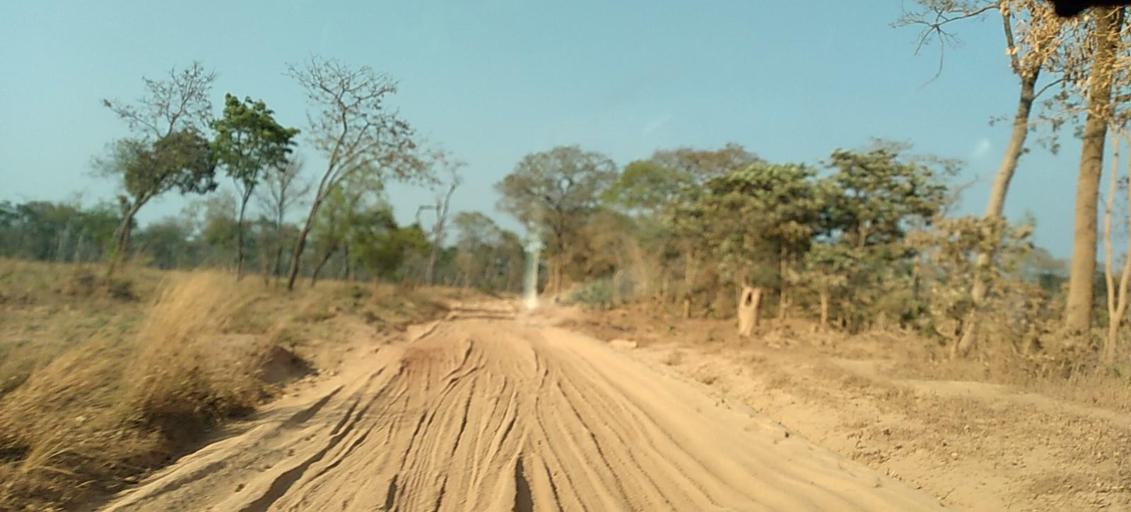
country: ZM
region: North-Western
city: Kasempa
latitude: -13.5715
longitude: 25.9939
